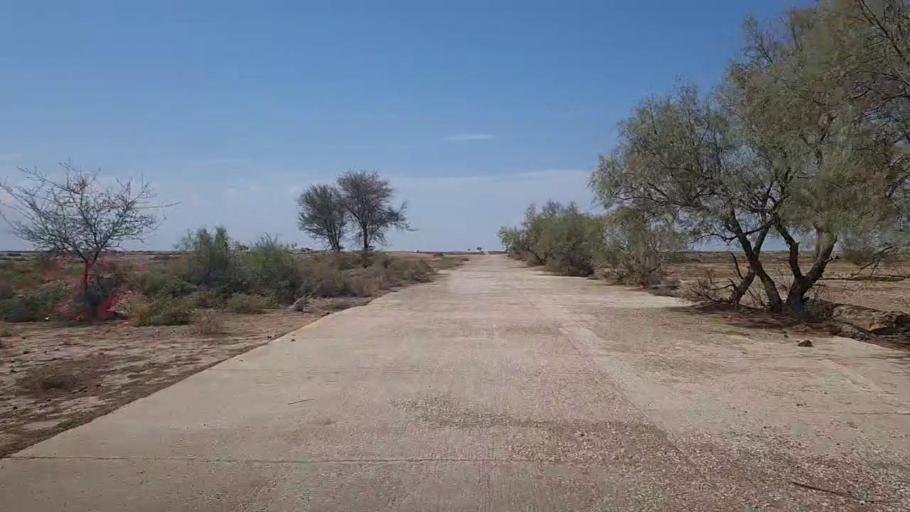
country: PK
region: Sindh
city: Sehwan
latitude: 26.3547
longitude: 67.6713
